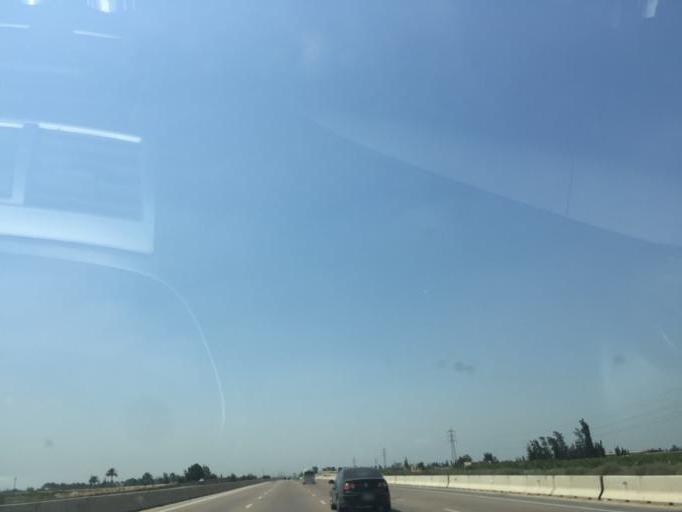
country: EG
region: Al Buhayrah
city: Abu al Matamir
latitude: 30.7529
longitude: 29.9940
